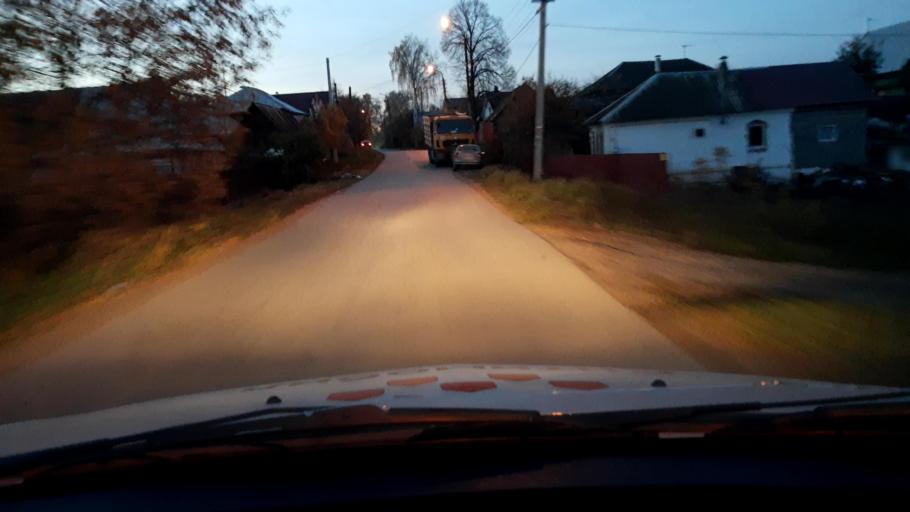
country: RU
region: Bashkortostan
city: Iglino
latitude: 54.7658
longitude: 56.2277
